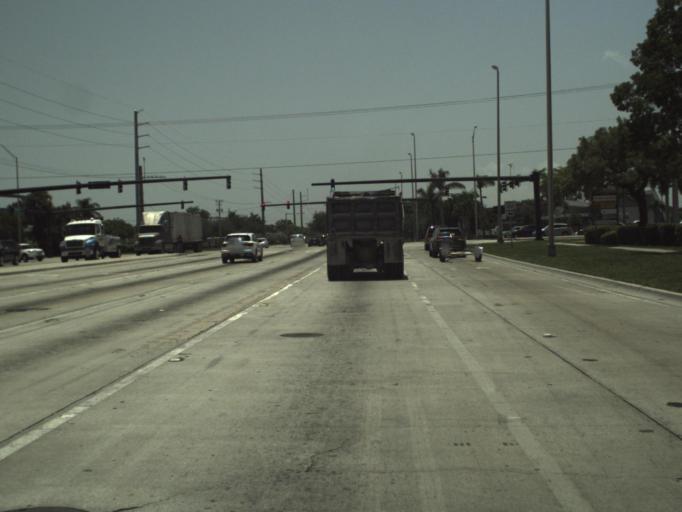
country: US
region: Florida
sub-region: Broward County
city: Tedder
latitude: 26.2755
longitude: -80.1523
